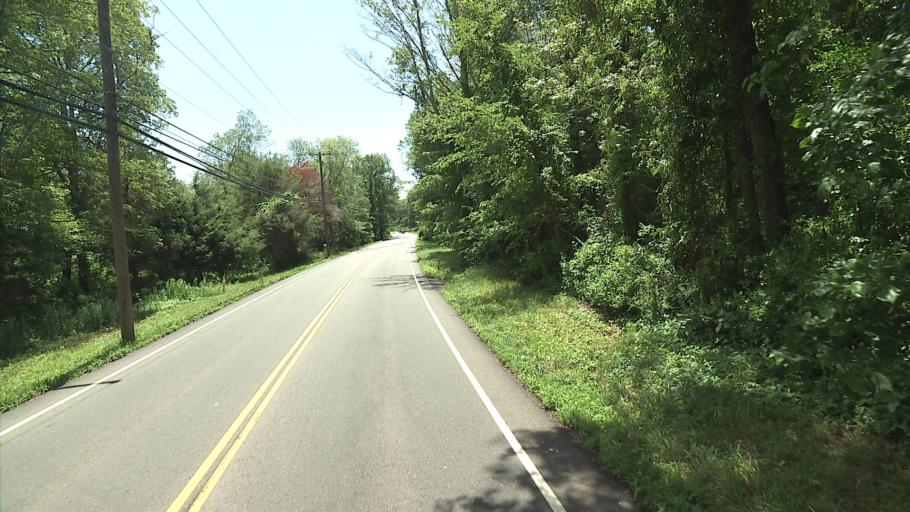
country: US
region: Connecticut
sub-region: Middlesex County
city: East Haddam
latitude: 41.4688
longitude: -72.4440
